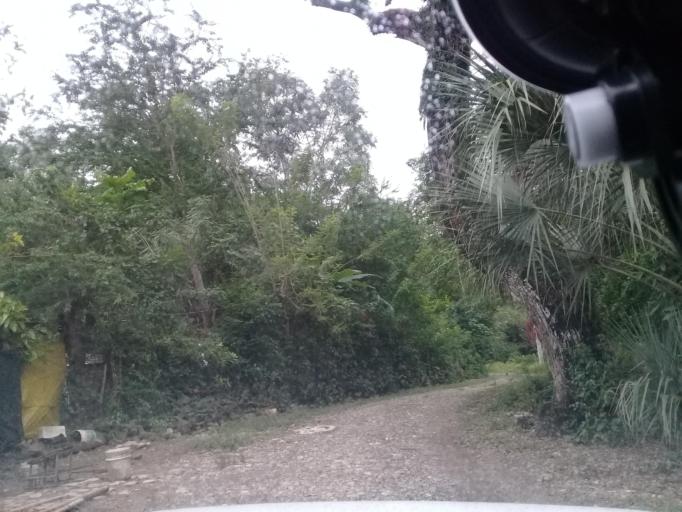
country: MX
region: Veracruz
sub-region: Chalma
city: San Pedro Coyutla
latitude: 21.2057
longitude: -98.3957
